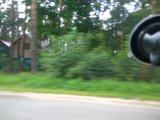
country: RU
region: Moskovskaya
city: Kratovo
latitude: 55.5881
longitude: 38.1508
